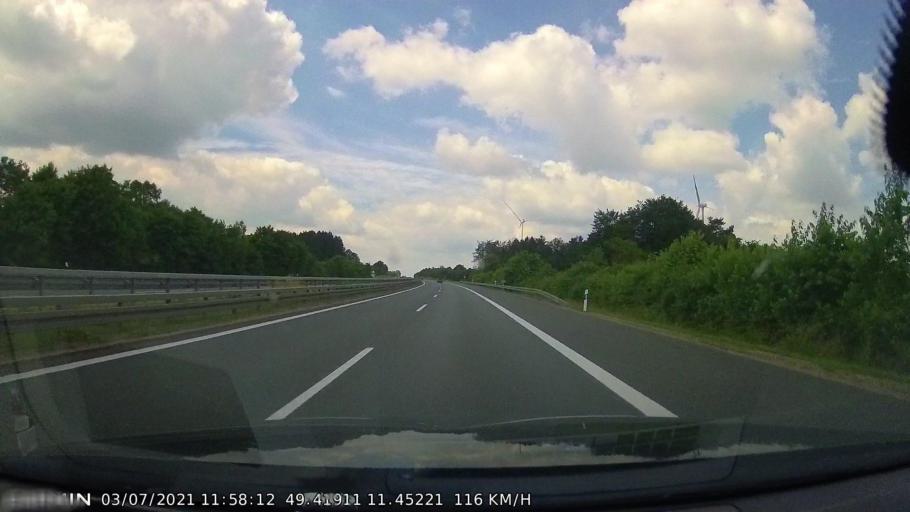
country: DE
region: Bavaria
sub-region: Regierungsbezirk Mittelfranken
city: Offenhausen
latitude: 49.4191
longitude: 11.4522
